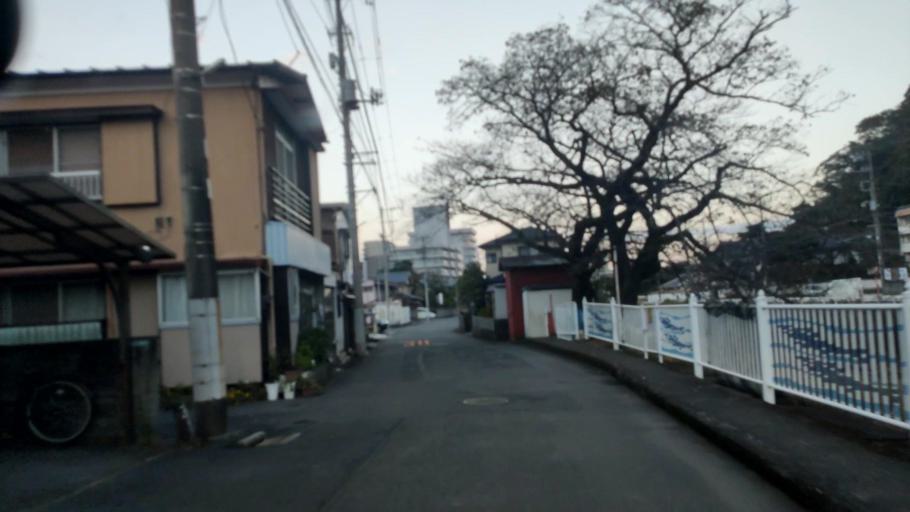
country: JP
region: Shizuoka
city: Ito
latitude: 34.9631
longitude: 139.0927
